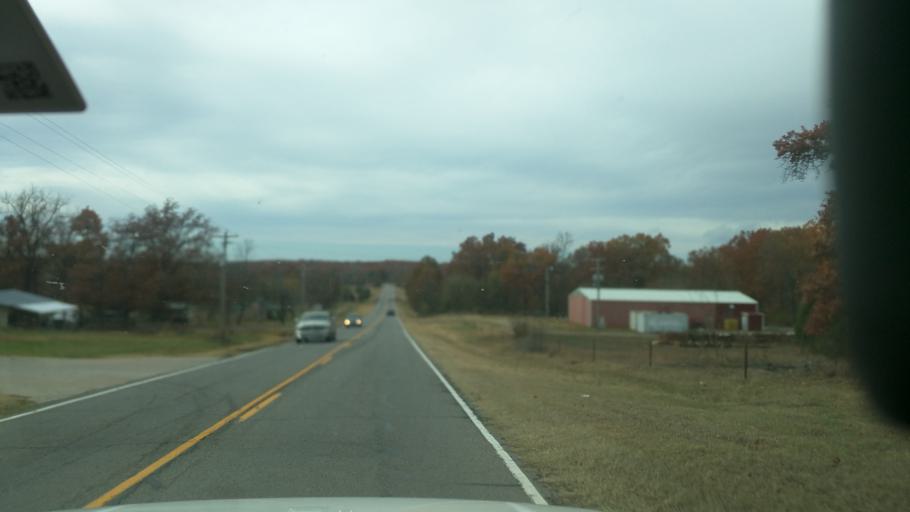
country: US
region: Oklahoma
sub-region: Cherokee County
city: Tahlequah
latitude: 35.9300
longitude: -94.8578
